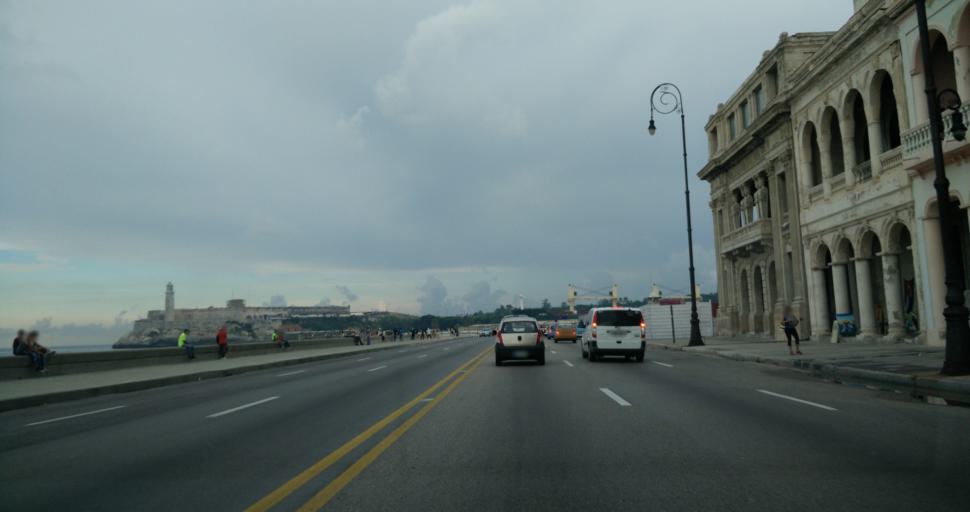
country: CU
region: La Habana
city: Centro Habana
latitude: 23.1448
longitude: -82.3597
